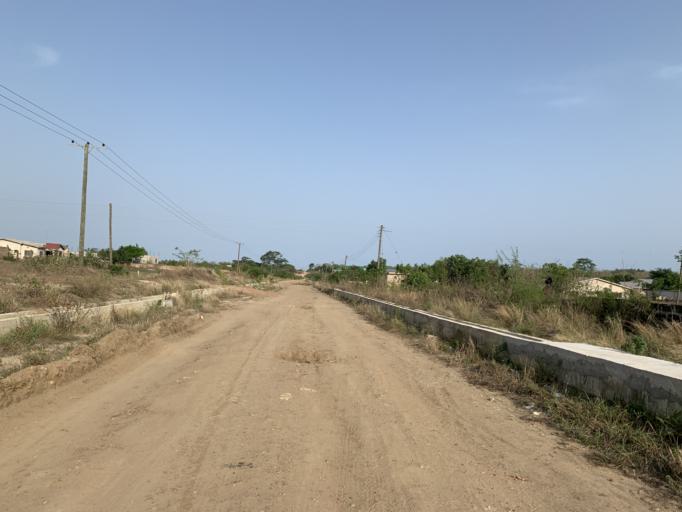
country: GH
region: Central
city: Winneba
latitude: 5.3813
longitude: -0.6220
